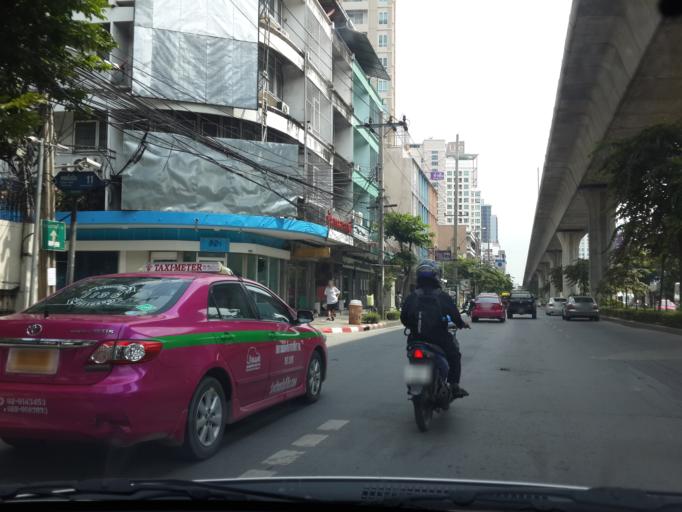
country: TH
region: Bangkok
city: Phaya Thai
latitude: 13.7868
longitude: 100.5472
